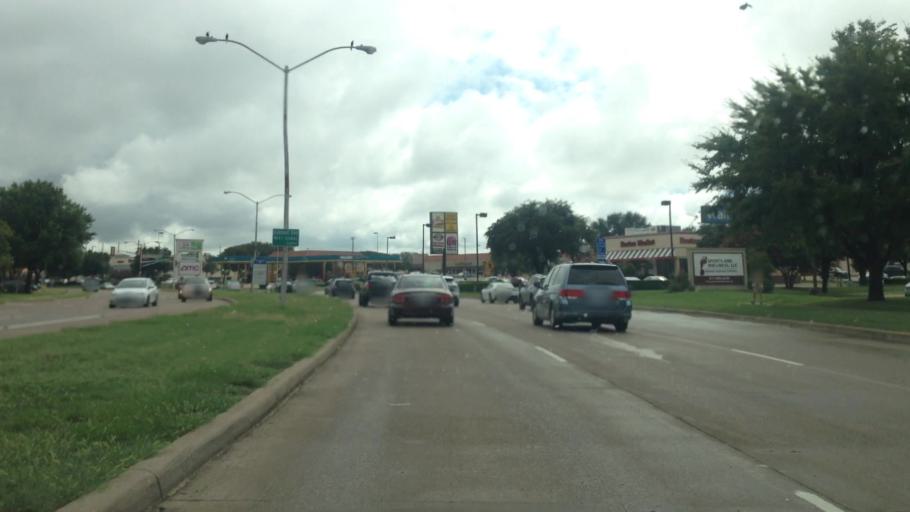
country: US
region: Texas
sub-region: Tarrant County
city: Benbrook
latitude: 32.6645
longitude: -97.4021
